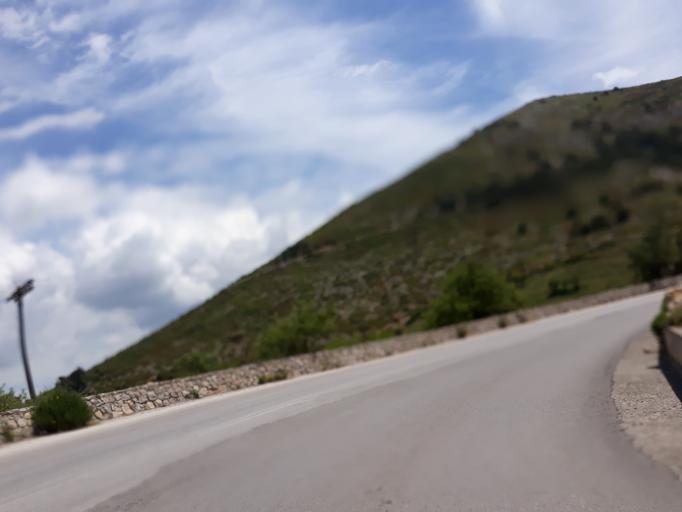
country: GR
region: Attica
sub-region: Nomarchia Dytikis Attikis
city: Magoula
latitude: 38.1721
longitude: 23.5461
